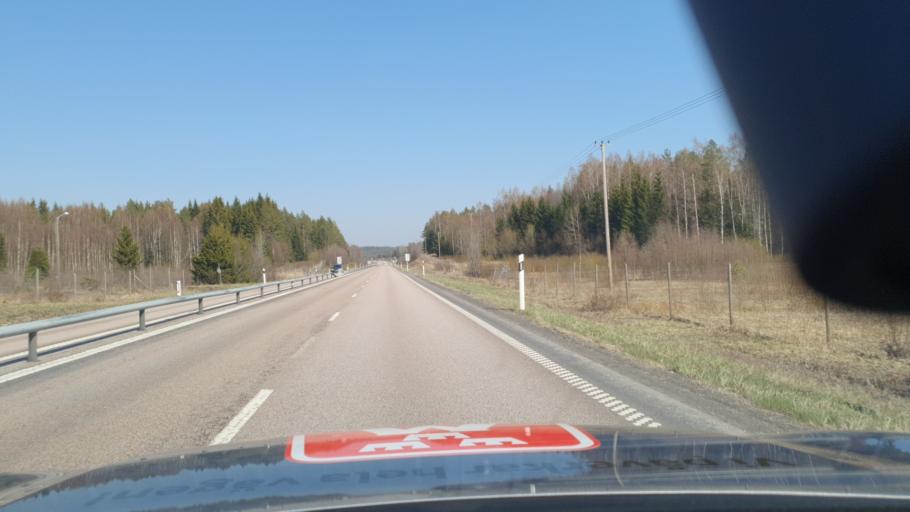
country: SE
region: Vaesternorrland
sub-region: OErnskoeldsviks Kommun
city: Husum
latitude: 63.3196
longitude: 19.0262
